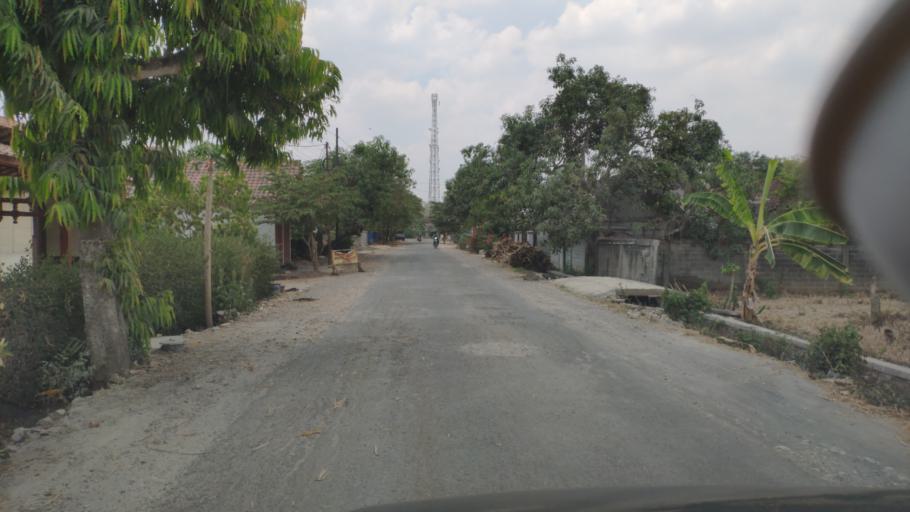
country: ID
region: Central Java
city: Banjarejo
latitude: -7.0314
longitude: 111.3479
